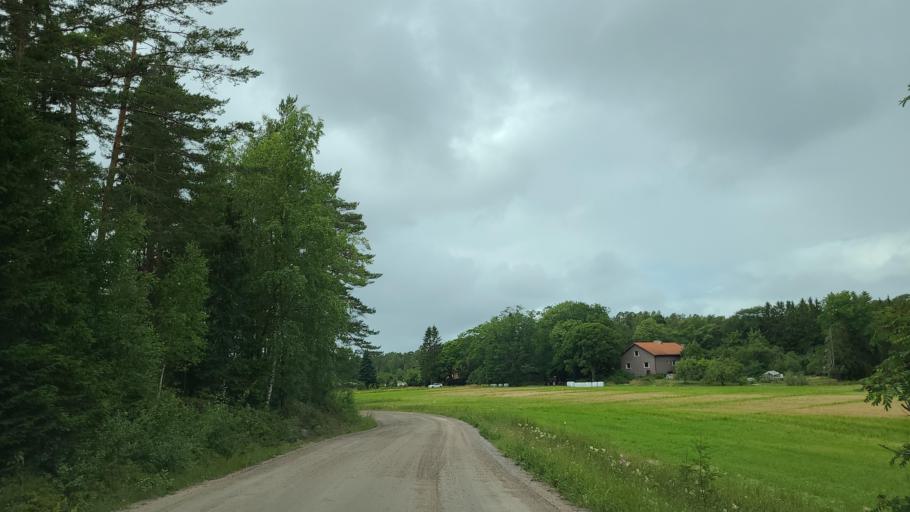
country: FI
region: Varsinais-Suomi
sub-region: Aboland-Turunmaa
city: Nagu
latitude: 60.2014
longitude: 21.8846
